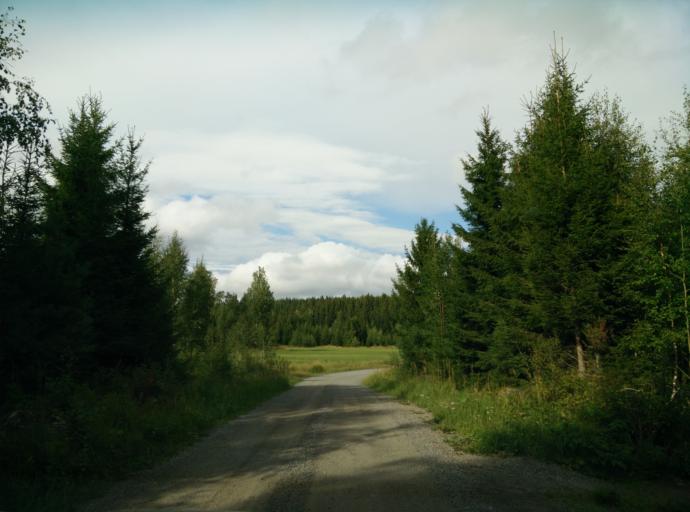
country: FI
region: Haeme
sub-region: Haemeenlinna
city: Kalvola
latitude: 61.1305
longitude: 24.1435
